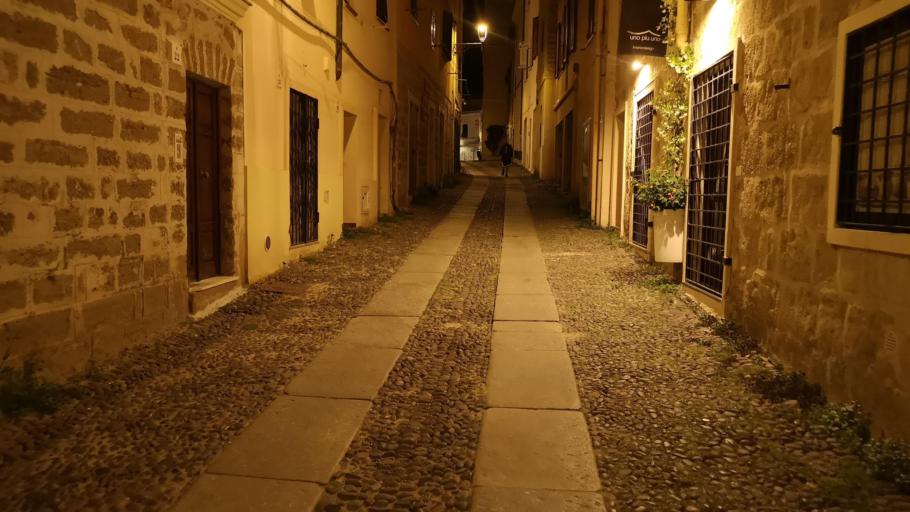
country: IT
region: Sardinia
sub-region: Provincia di Sassari
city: Alghero
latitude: 40.5589
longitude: 8.3143
